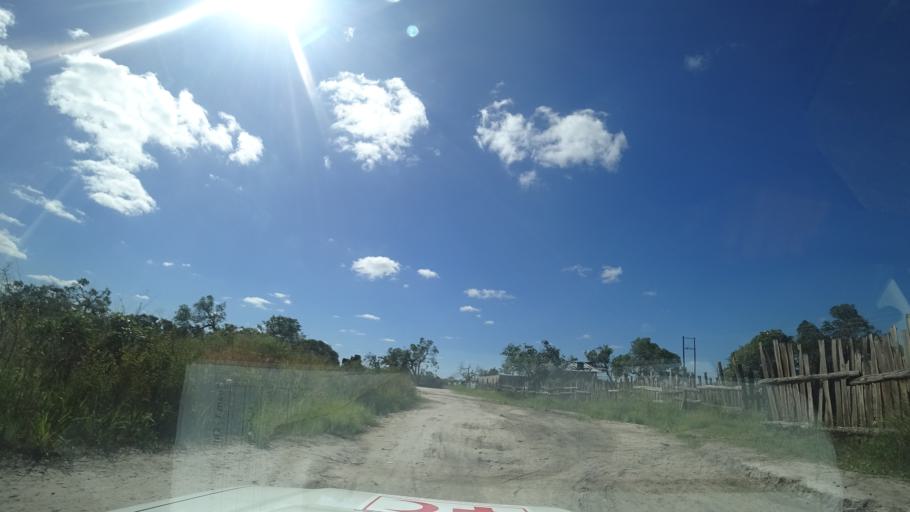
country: MZ
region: Sofala
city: Dondo
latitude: -19.5012
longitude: 34.6126
